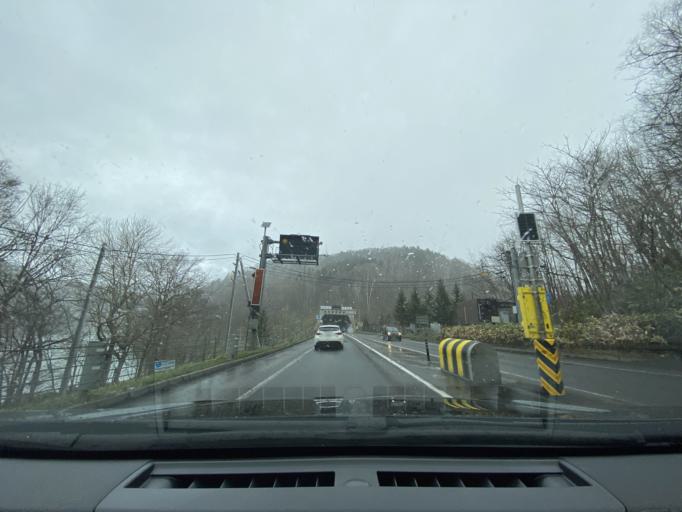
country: JP
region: Hokkaido
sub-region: Asahikawa-shi
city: Asahikawa
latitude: 43.7381
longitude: 142.2423
